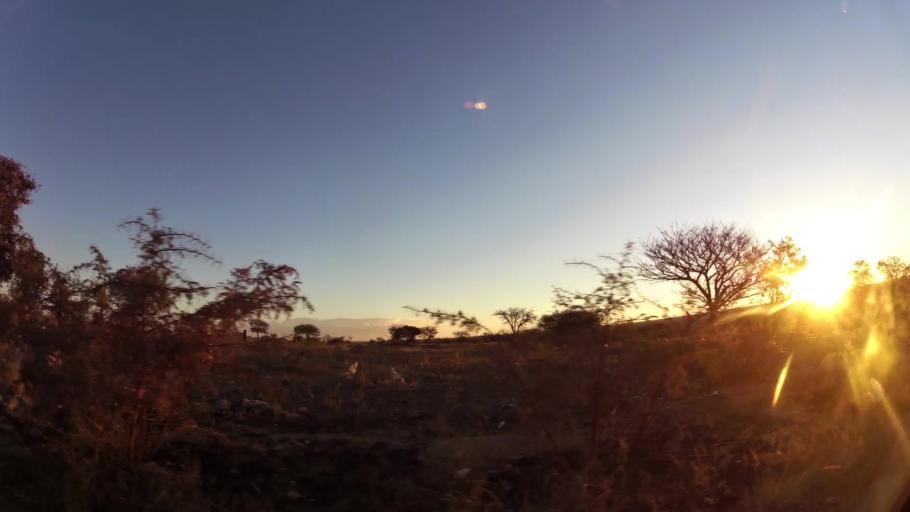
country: ZA
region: Limpopo
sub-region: Capricorn District Municipality
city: Polokwane
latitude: -23.8580
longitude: 29.3629
